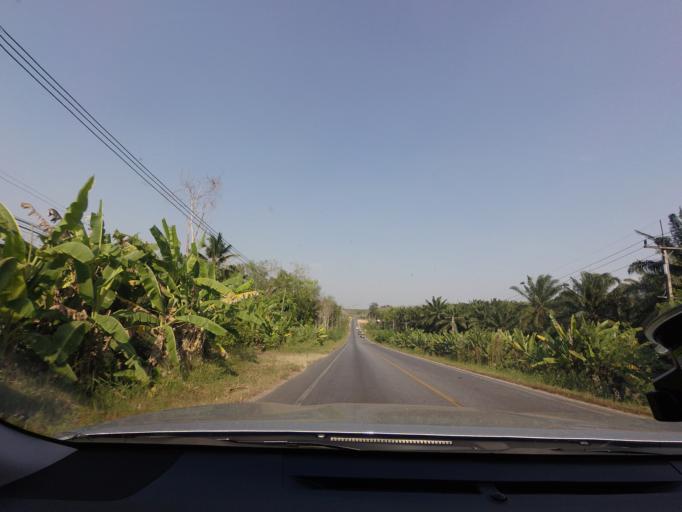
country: TH
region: Surat Thani
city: Chai Buri
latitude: 8.5704
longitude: 99.1229
